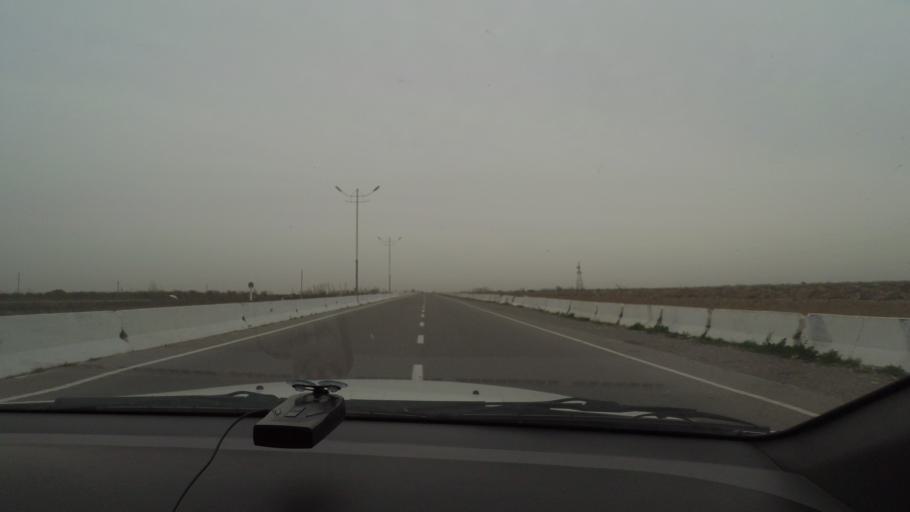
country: UZ
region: Jizzax
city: Dustlik
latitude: 40.4174
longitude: 68.2099
